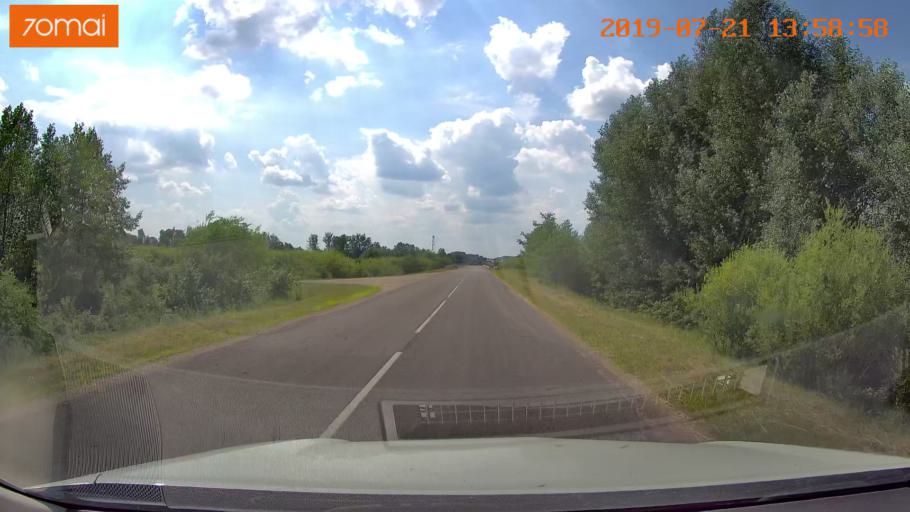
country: BY
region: Grodnenskaya
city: Lyubcha
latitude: 53.7567
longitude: 26.0694
